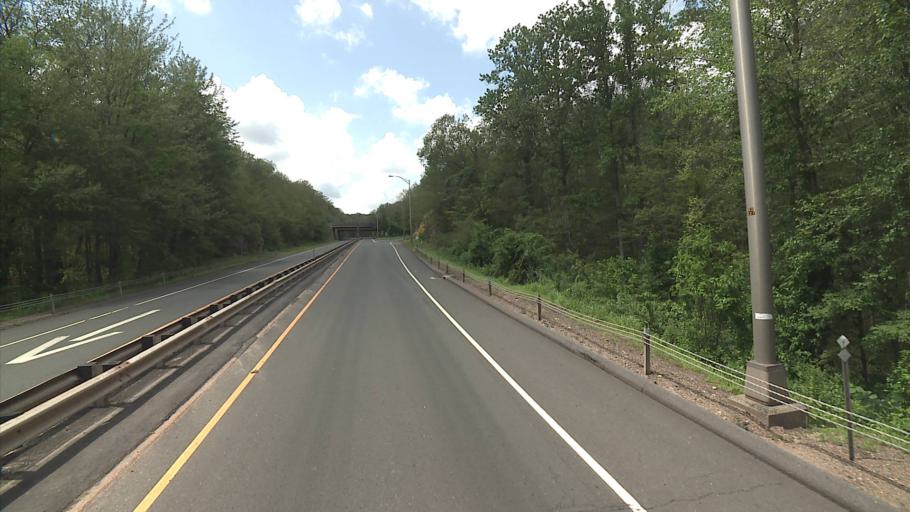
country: US
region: Connecticut
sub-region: Middlesex County
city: Higganum
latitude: 41.5125
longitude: -72.5949
